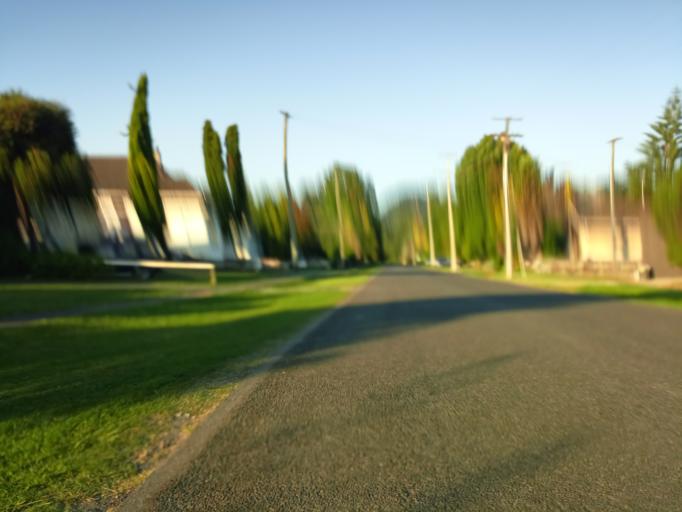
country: NZ
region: Gisborne
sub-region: Gisborne District
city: Gisborne
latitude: -38.6487
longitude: 178.0112
